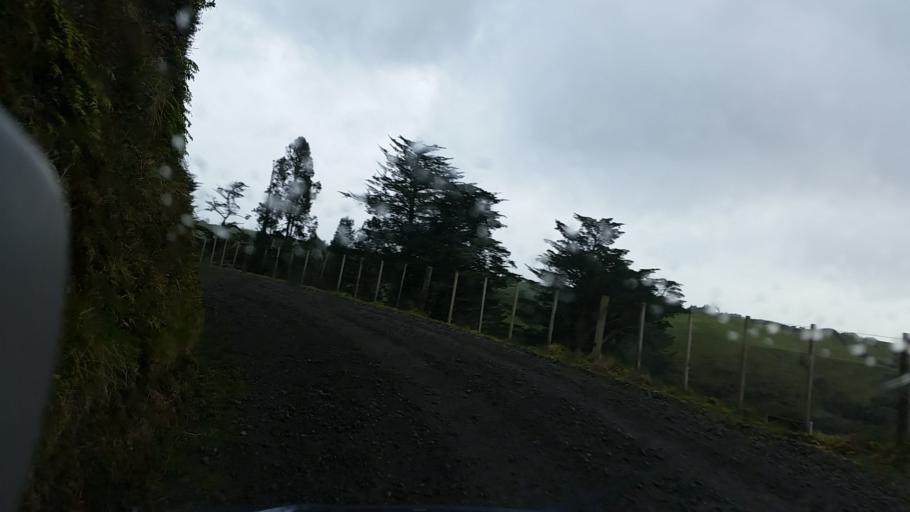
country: NZ
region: Taranaki
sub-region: South Taranaki District
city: Eltham
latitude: -39.2805
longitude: 174.3363
